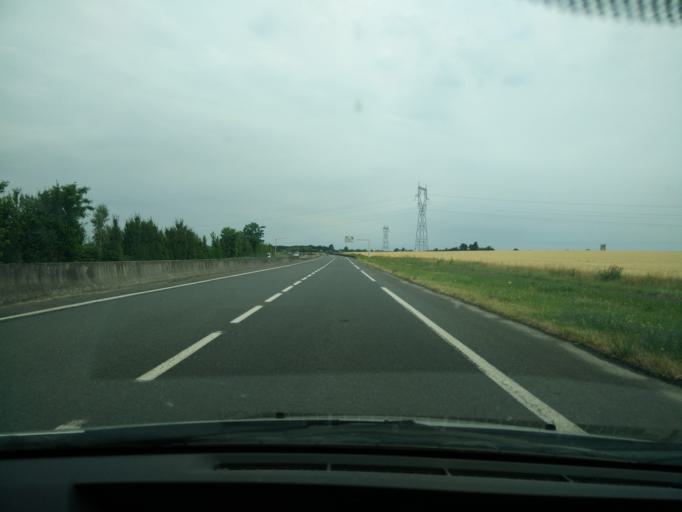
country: FR
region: Pays de la Loire
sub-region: Departement de Maine-et-Loire
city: Doue-la-Fontaine
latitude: 47.2263
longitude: -0.3080
